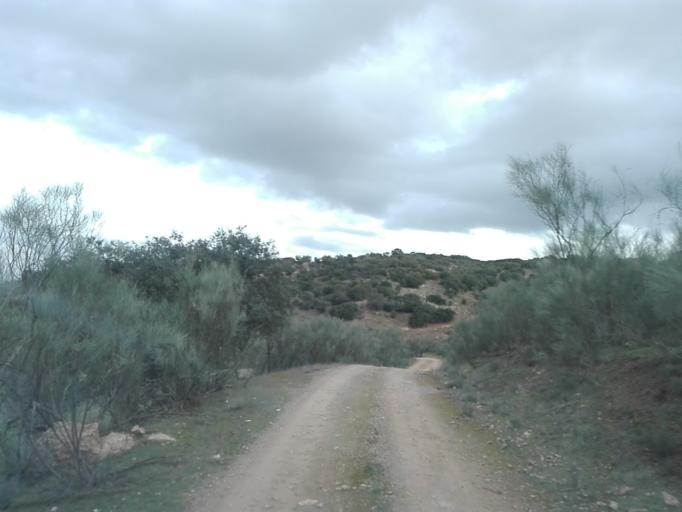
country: ES
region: Extremadura
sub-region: Provincia de Badajoz
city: Hinojosa del Valle
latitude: 38.4416
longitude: -6.1862
